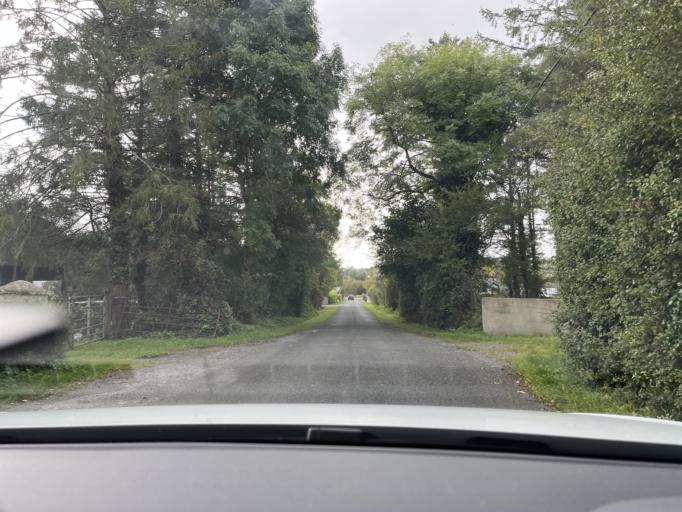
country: IE
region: Connaught
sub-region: County Leitrim
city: Carrick-on-Shannon
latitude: 53.9624
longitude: -8.0866
